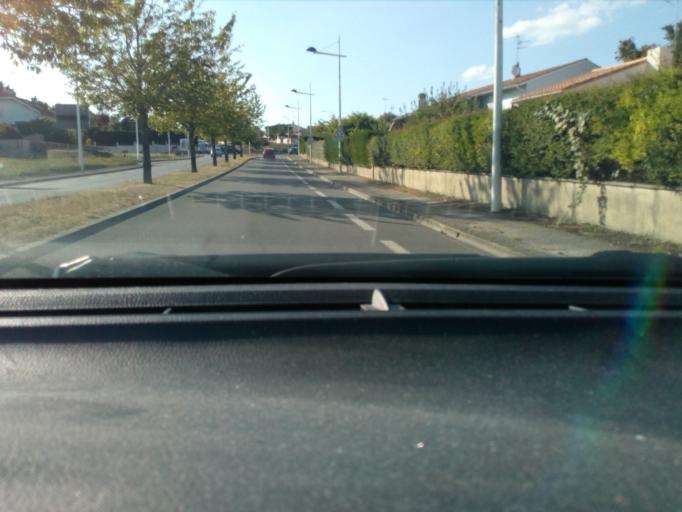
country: FR
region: Poitou-Charentes
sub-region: Departement de la Charente
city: Angouleme
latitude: 45.6637
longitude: 0.1532
